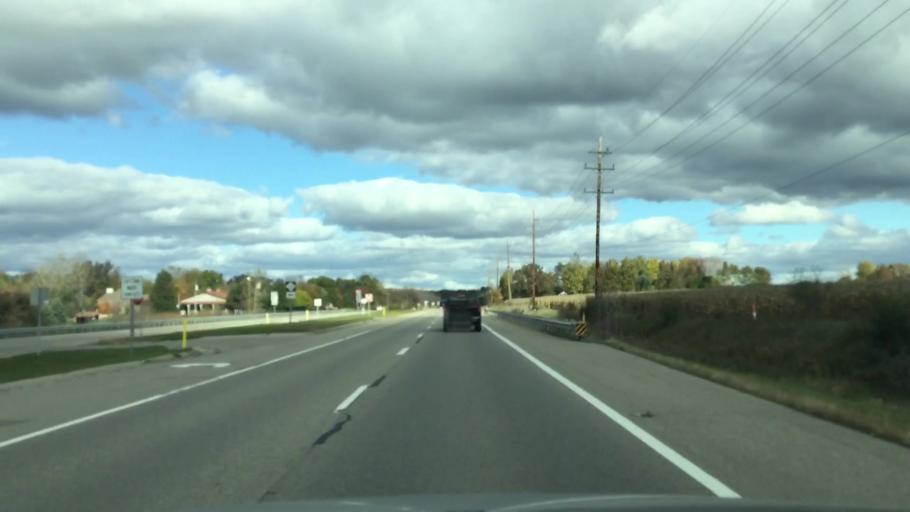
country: US
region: Michigan
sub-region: Lapeer County
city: Lapeer
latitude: 42.9795
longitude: -83.3152
